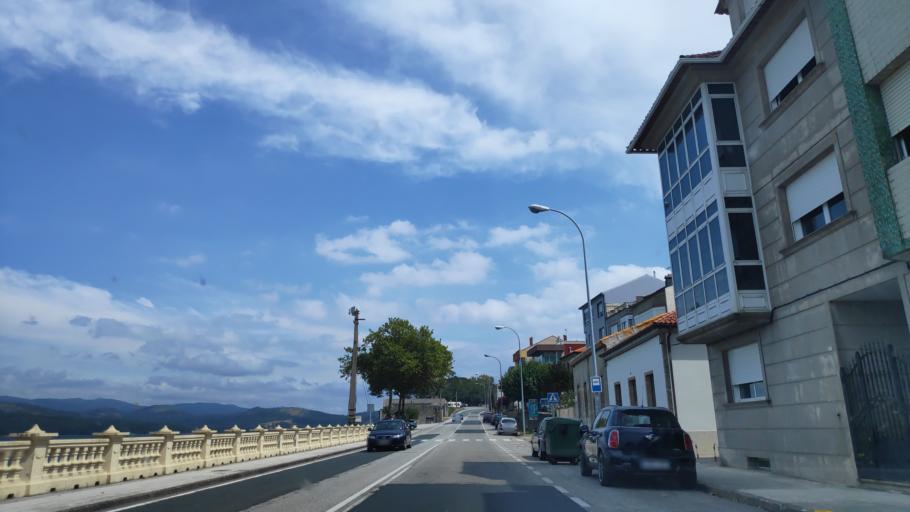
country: ES
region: Galicia
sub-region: Provincia de Pontevedra
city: Vilagarcia de Arousa
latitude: 42.6170
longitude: -8.7755
